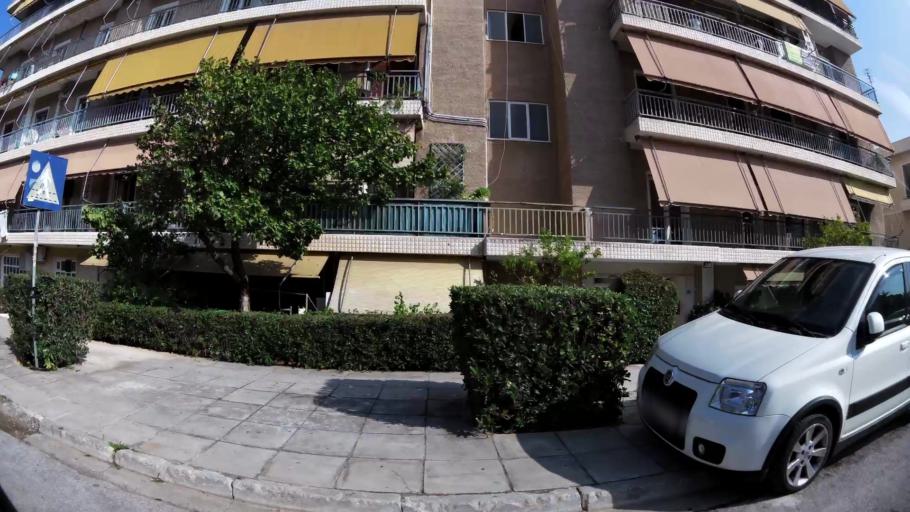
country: GR
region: Attica
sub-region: Nomarchia Athinas
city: Argyroupoli
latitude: 37.9224
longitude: 23.7475
